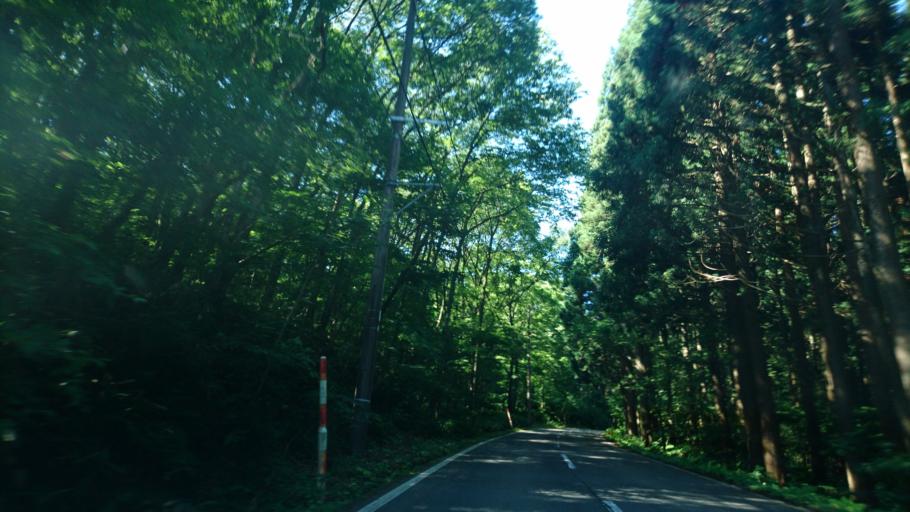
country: JP
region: Akita
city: Kakunodatemachi
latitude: 39.7235
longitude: 140.6985
